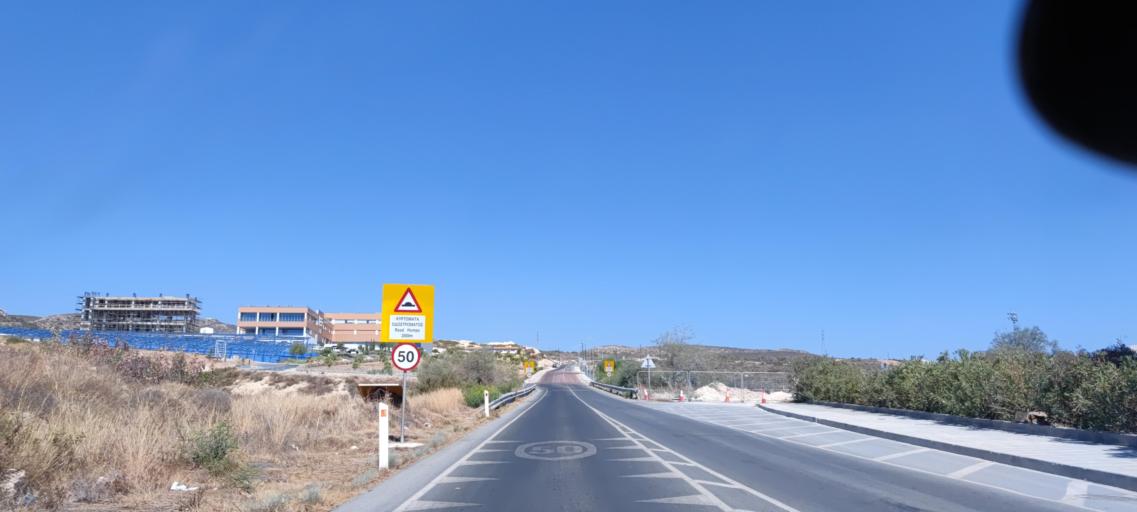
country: CY
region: Limassol
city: Mouttagiaka
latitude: 34.7272
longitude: 33.0613
